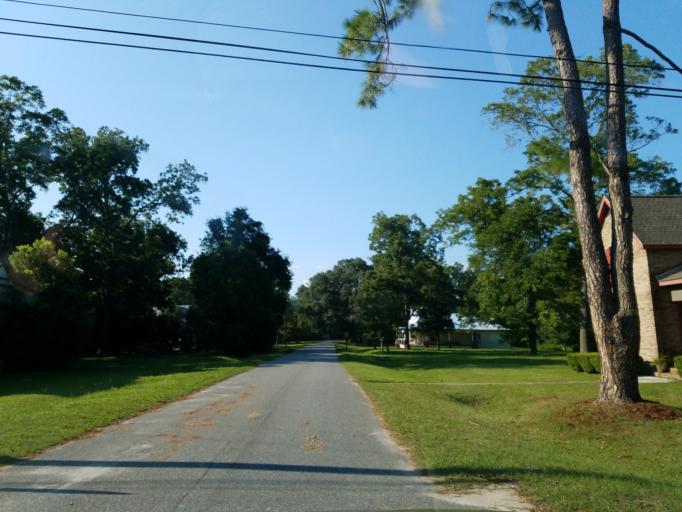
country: US
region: Georgia
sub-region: Lowndes County
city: Hahira
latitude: 31.0464
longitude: -83.3945
